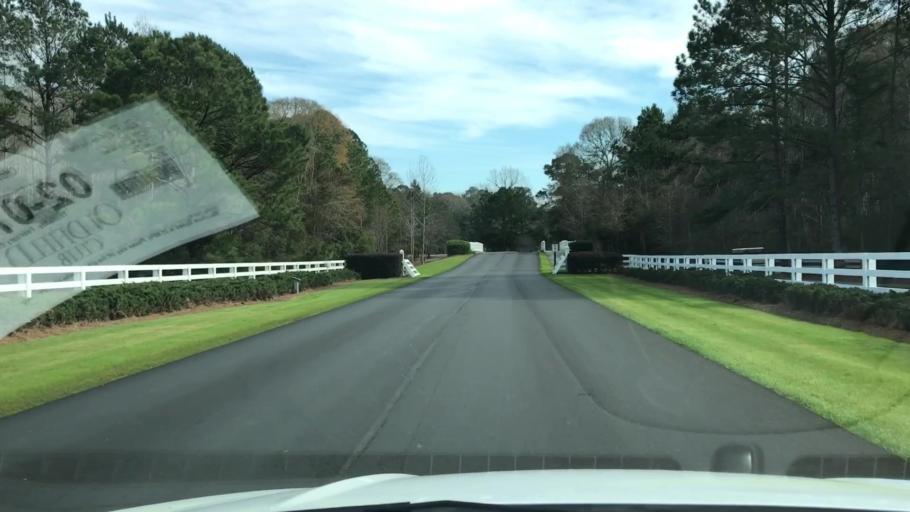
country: US
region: South Carolina
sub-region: Beaufort County
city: Bluffton
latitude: 32.3444
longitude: -80.9213
